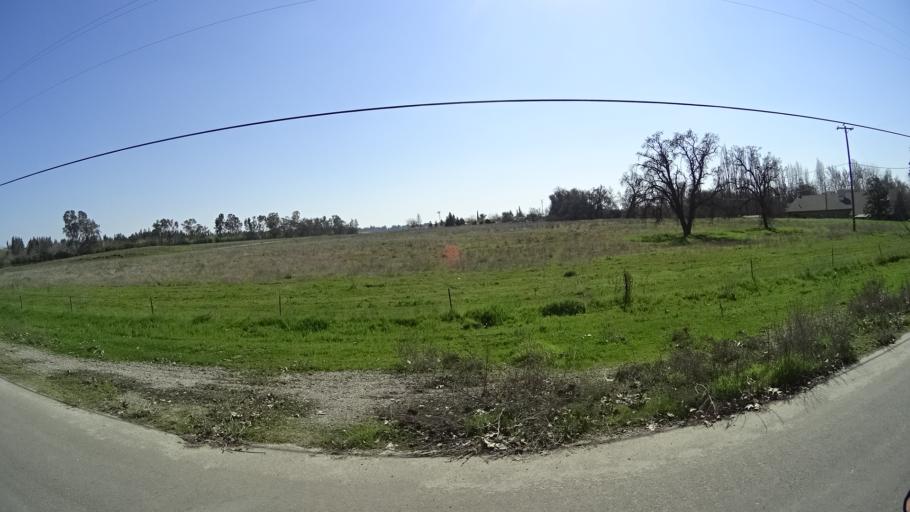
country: US
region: California
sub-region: Fresno County
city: Clovis
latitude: 36.8884
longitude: -119.7831
